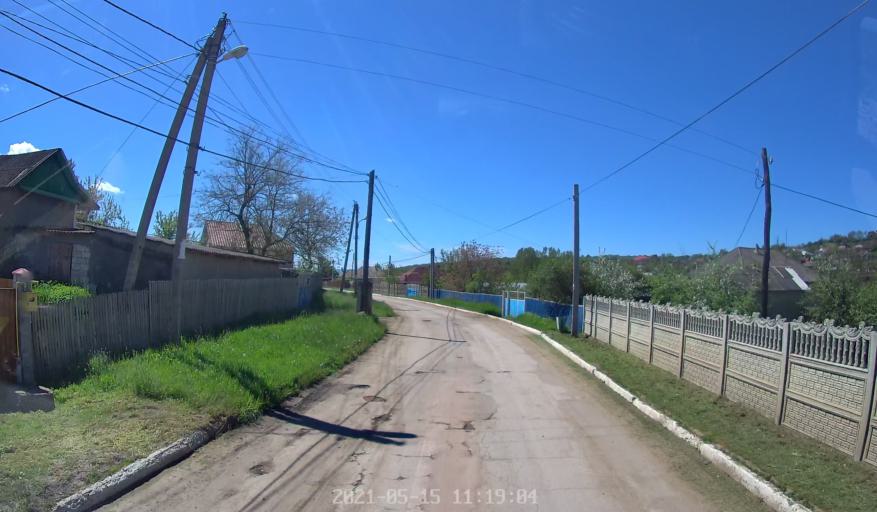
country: MD
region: Hincesti
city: Hincesti
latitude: 46.8329
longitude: 28.6759
